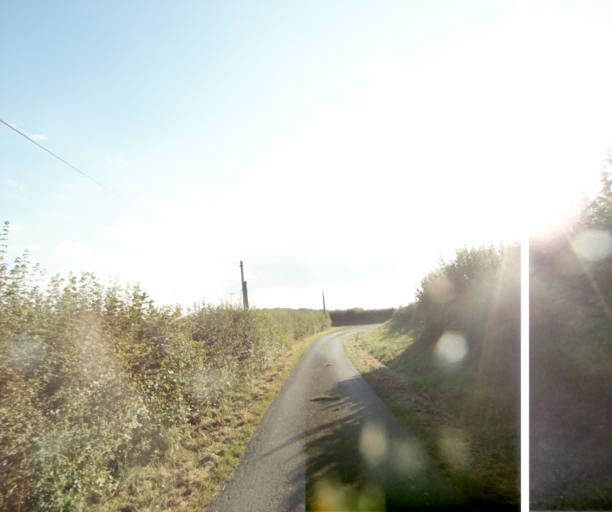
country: FR
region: Bourgogne
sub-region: Departement de Saone-et-Loire
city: Gueugnon
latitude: 46.5832
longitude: 4.1395
